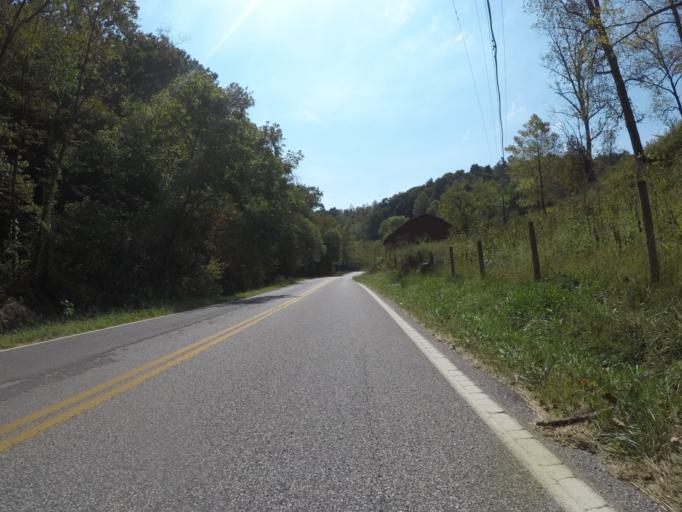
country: US
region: West Virginia
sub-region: Cabell County
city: Lesage
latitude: 38.5815
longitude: -82.4184
